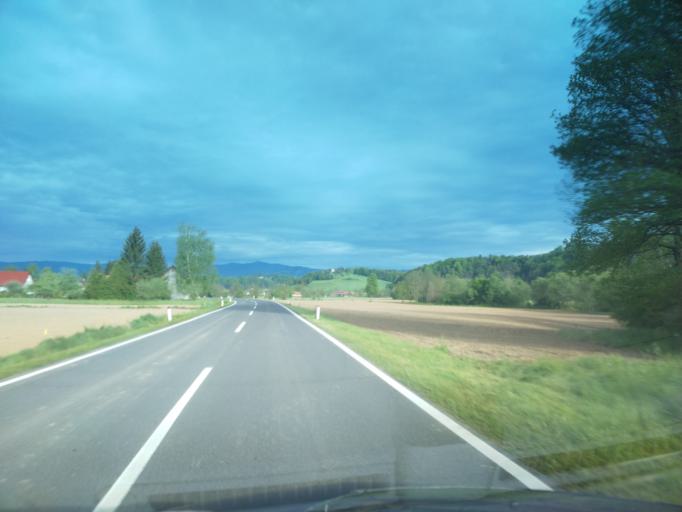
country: AT
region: Styria
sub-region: Politischer Bezirk Leibnitz
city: Oberhaag
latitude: 46.6983
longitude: 15.3040
